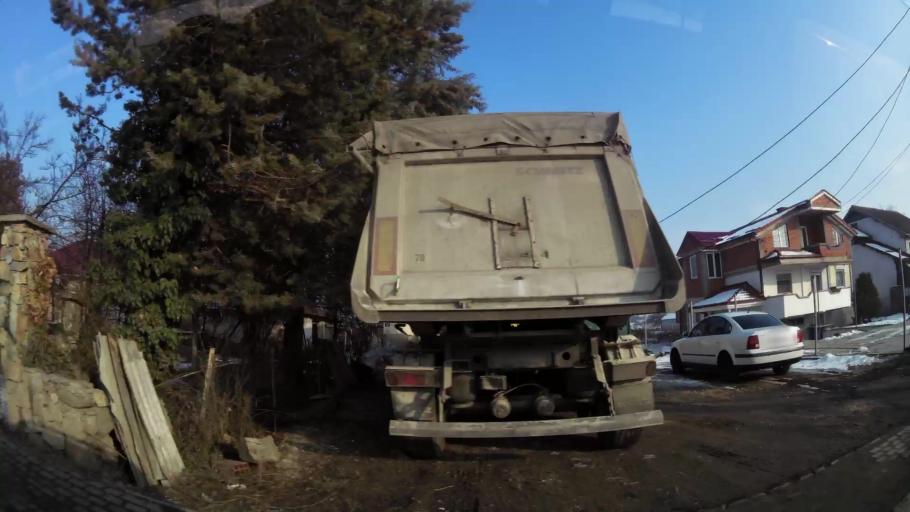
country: MK
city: Creshevo
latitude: 42.0237
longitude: 21.5149
